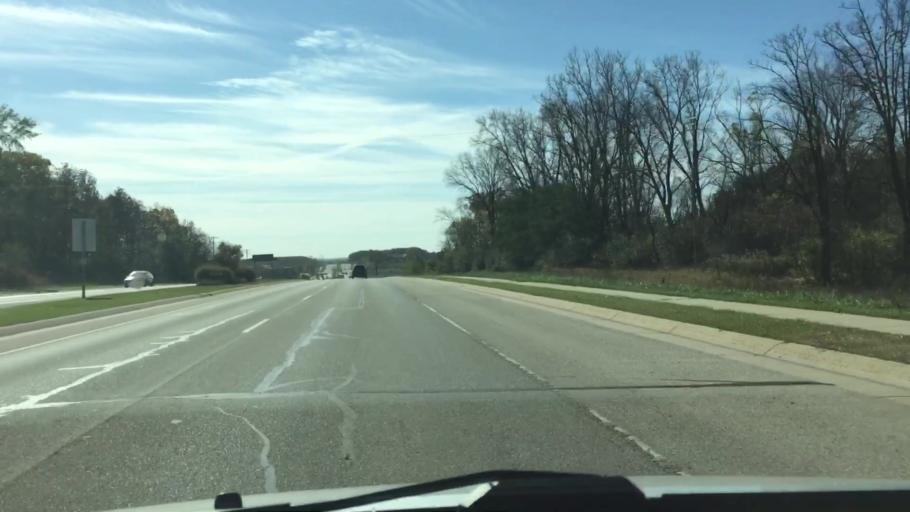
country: US
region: Wisconsin
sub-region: Waukesha County
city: Sussex
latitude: 43.1200
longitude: -88.2446
